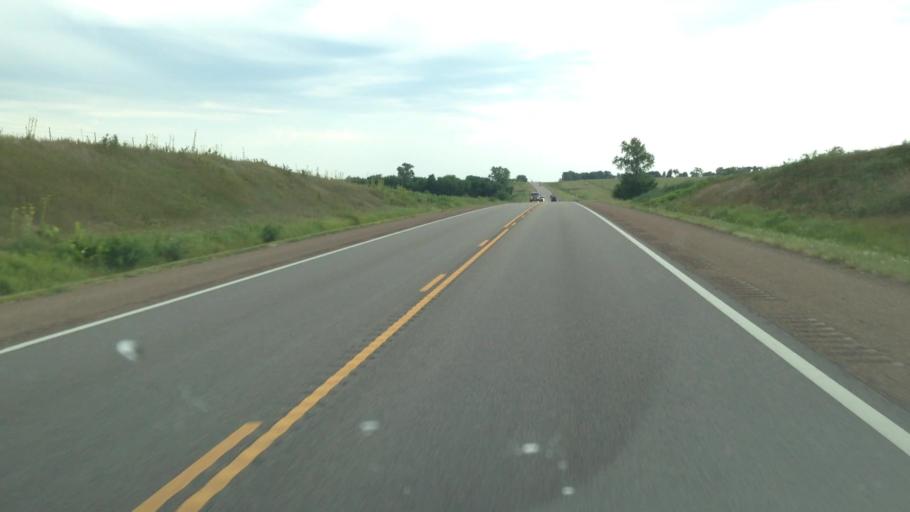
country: US
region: Kansas
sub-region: Woodson County
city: Yates Center
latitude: 38.0166
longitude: -95.7392
